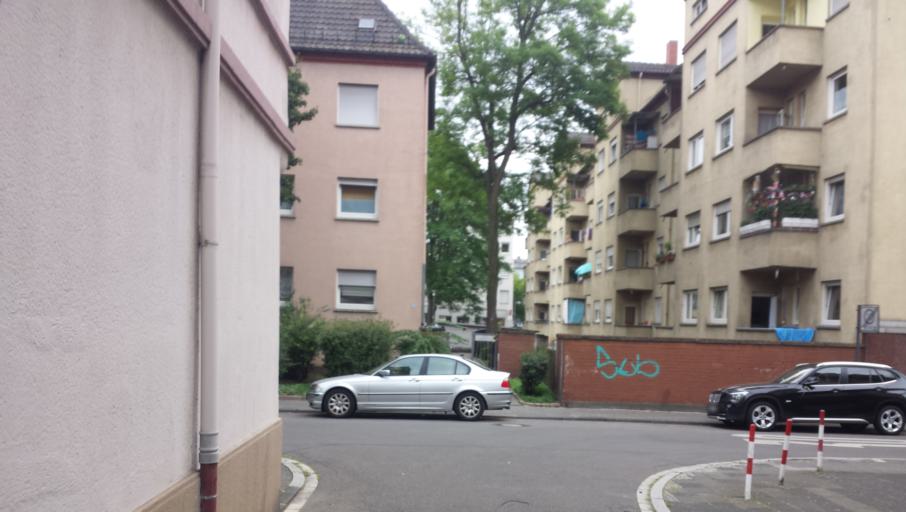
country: DE
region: Rheinland-Pfalz
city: Ludwigshafen am Rhein
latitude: 49.4901
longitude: 8.4314
